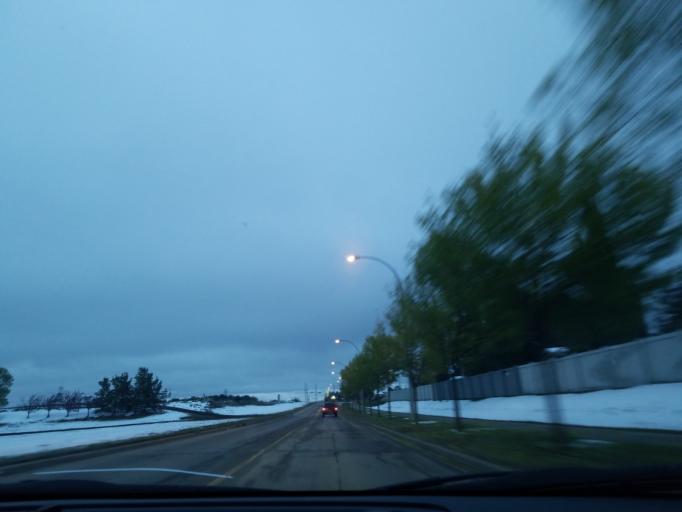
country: CA
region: Alberta
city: Edmonton
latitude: 53.6158
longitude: -113.3831
